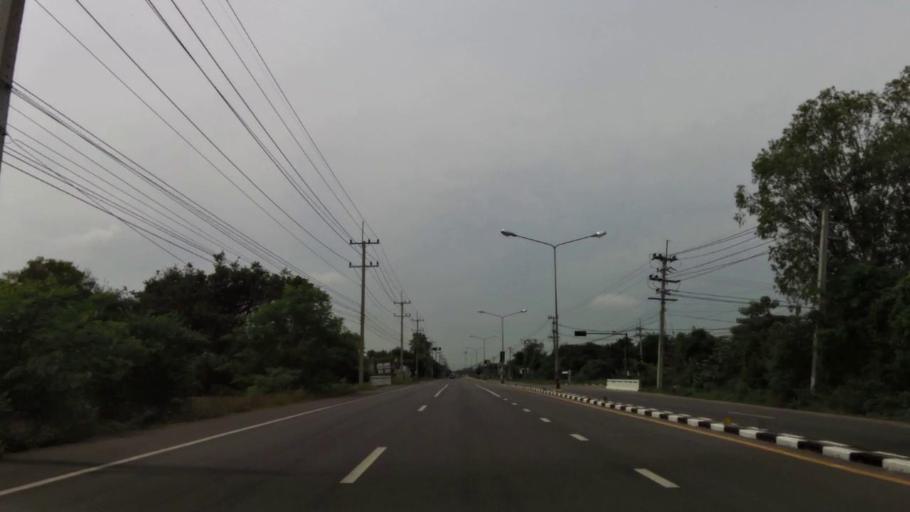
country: TH
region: Lop Buri
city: Ban Mi
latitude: 15.0569
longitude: 100.5890
